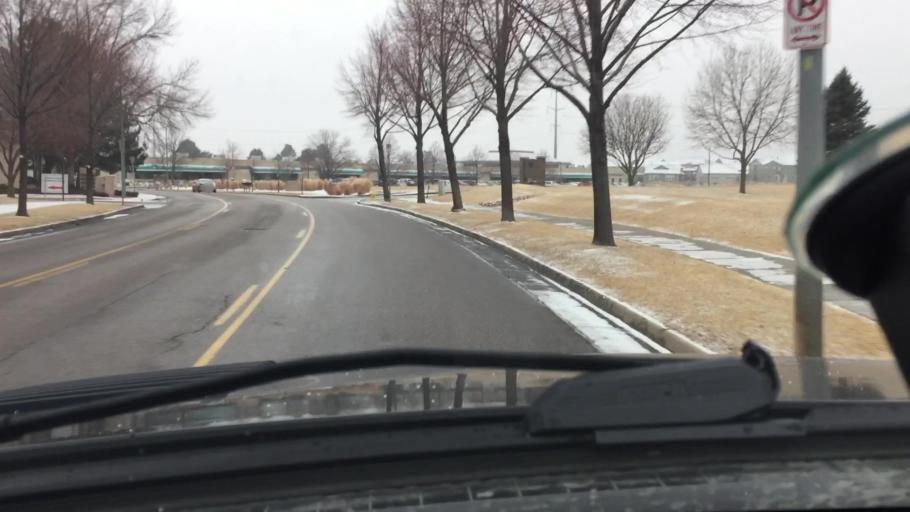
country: US
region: Colorado
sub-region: Larimer County
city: Fort Collins
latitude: 40.5634
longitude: -105.0321
